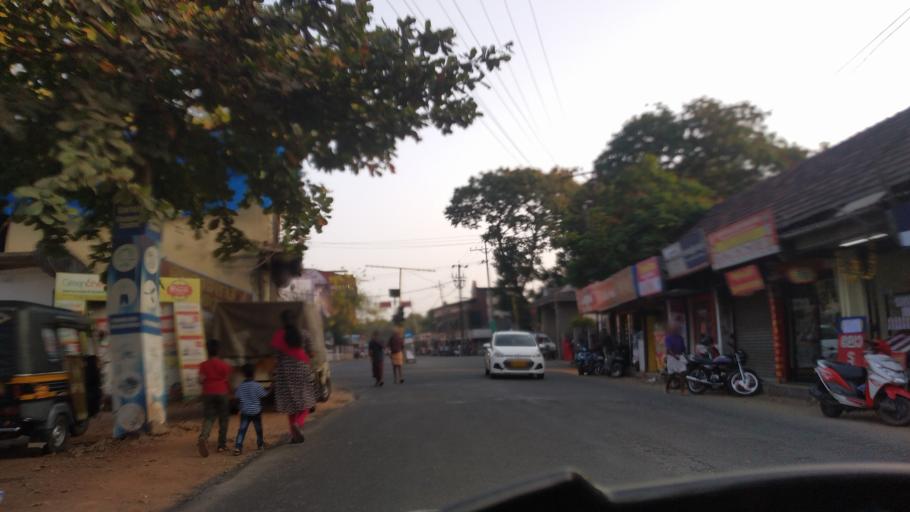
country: IN
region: Kerala
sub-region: Thrissur District
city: Kodungallur
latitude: 10.1490
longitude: 76.2242
